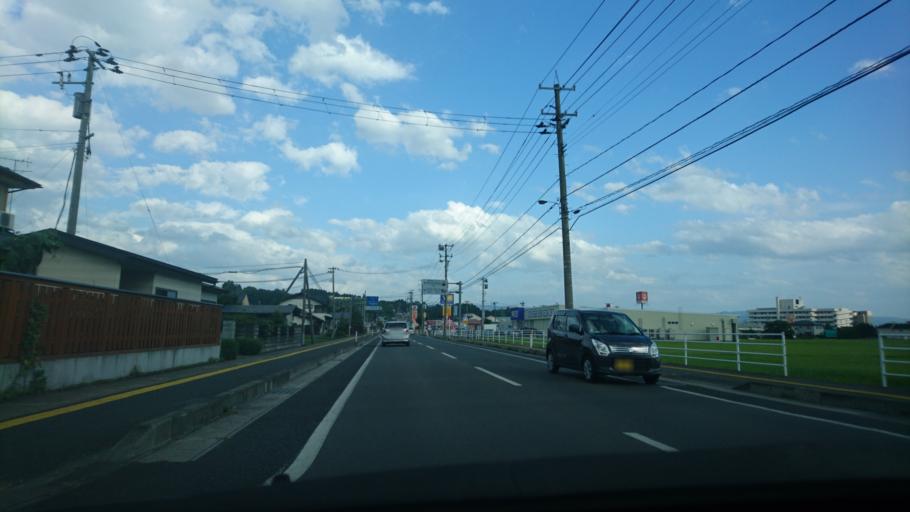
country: JP
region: Iwate
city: Mizusawa
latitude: 39.1984
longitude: 141.1694
